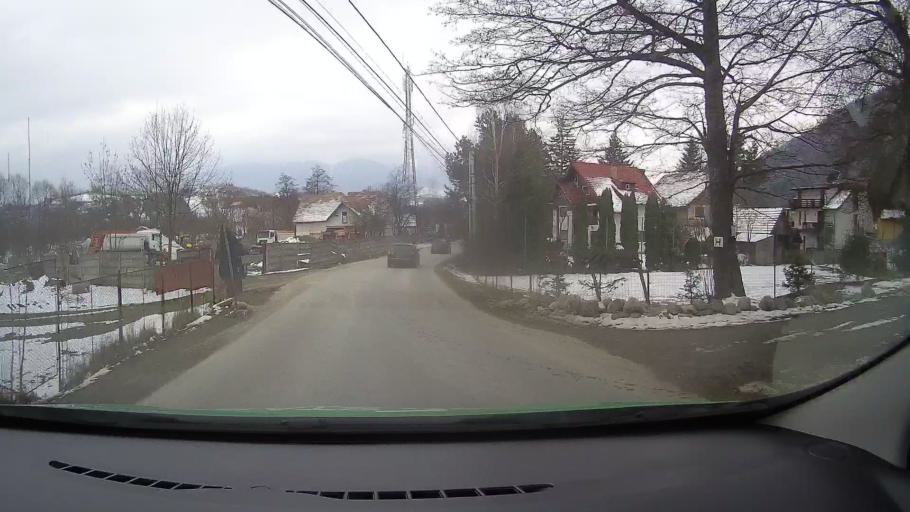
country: RO
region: Brasov
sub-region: Comuna Bran
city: Bran
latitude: 45.5244
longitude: 25.3651
